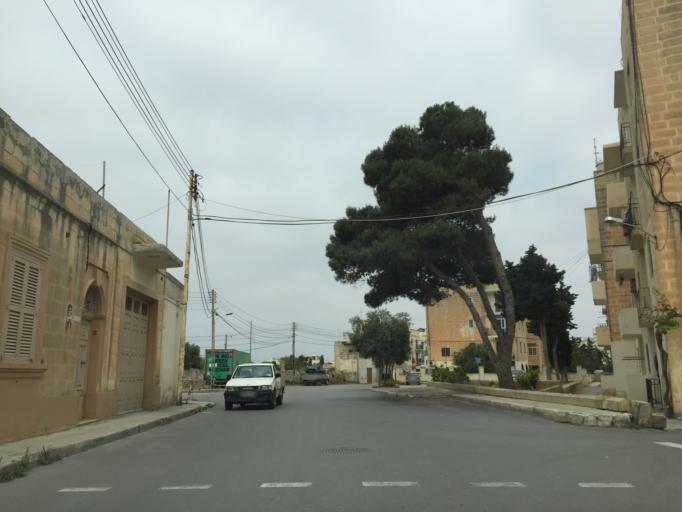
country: MT
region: Ir-Rabat
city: Rabat
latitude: 35.8829
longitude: 14.3909
